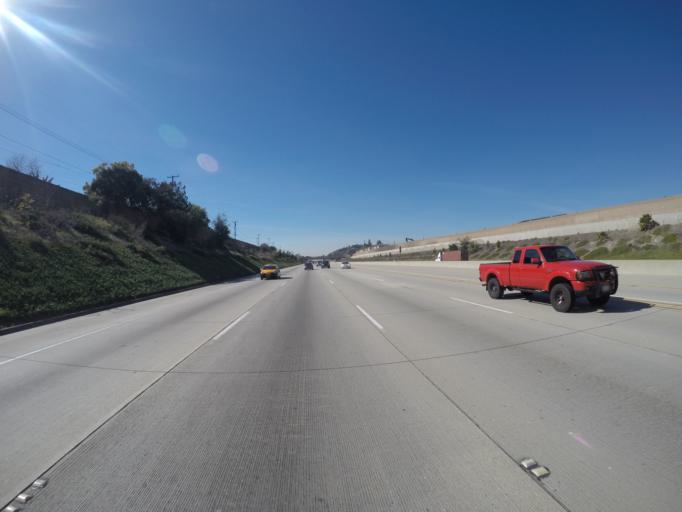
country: US
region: California
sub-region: Los Angeles County
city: Claremont
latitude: 34.1200
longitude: -117.7216
